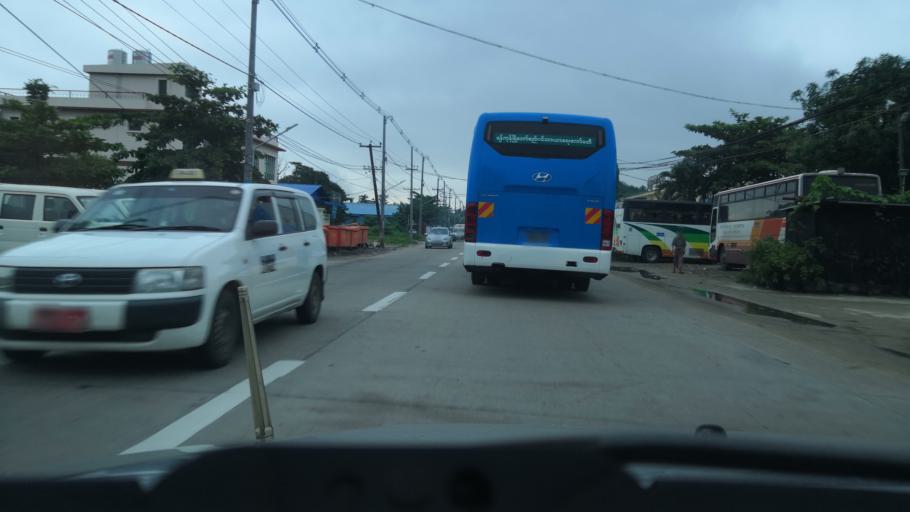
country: MM
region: Yangon
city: Yangon
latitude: 16.8848
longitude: 96.1678
